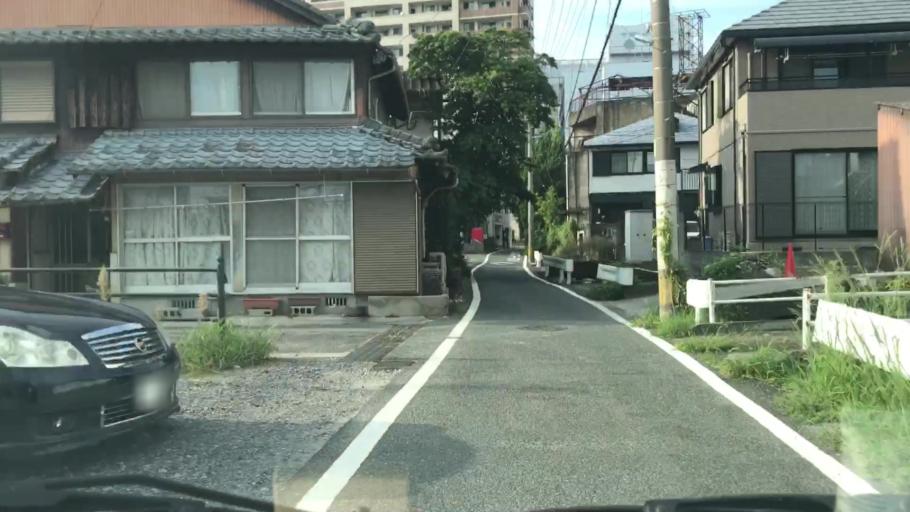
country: JP
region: Saga Prefecture
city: Saga-shi
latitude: 33.2606
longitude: 130.2973
